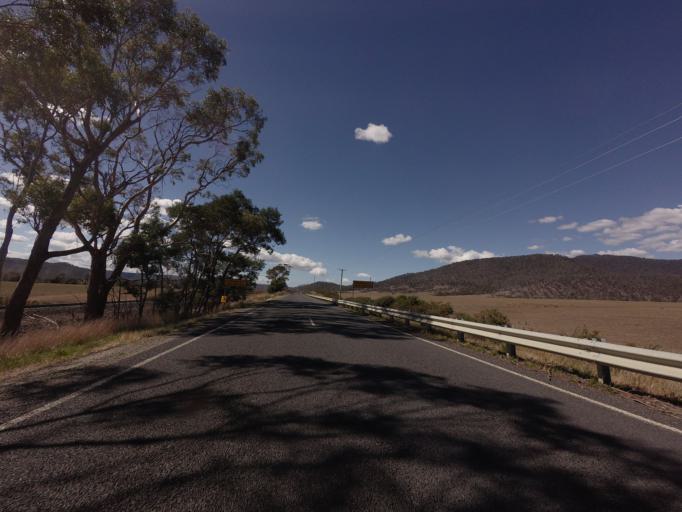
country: AU
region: Tasmania
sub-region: Break O'Day
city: St Helens
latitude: -41.6771
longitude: 147.8938
